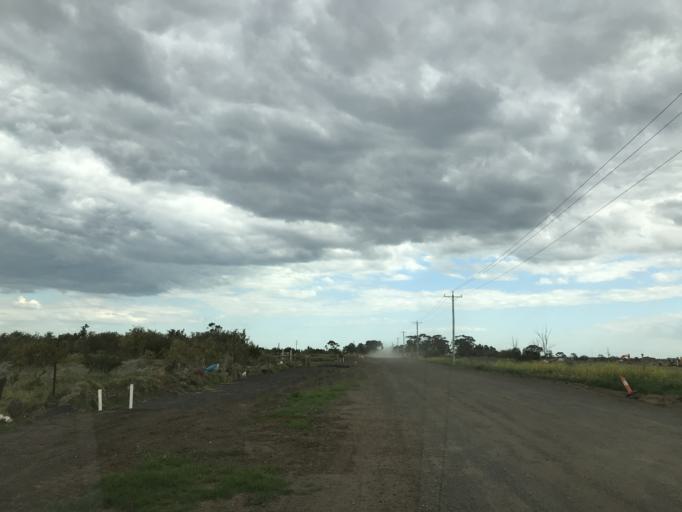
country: AU
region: Victoria
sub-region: Wyndham
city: Truganina
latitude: -37.8174
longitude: 144.7222
